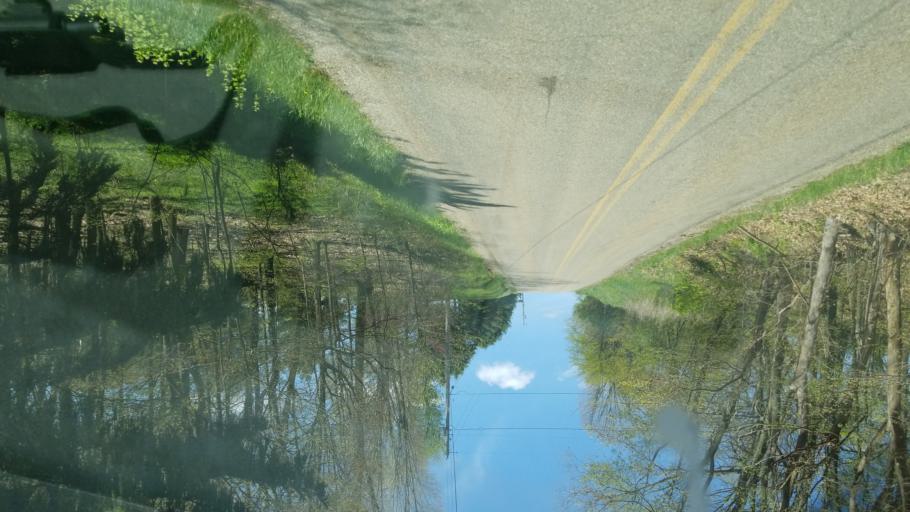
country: US
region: Ohio
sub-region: Richland County
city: Lincoln Heights
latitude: 40.7416
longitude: -82.4061
